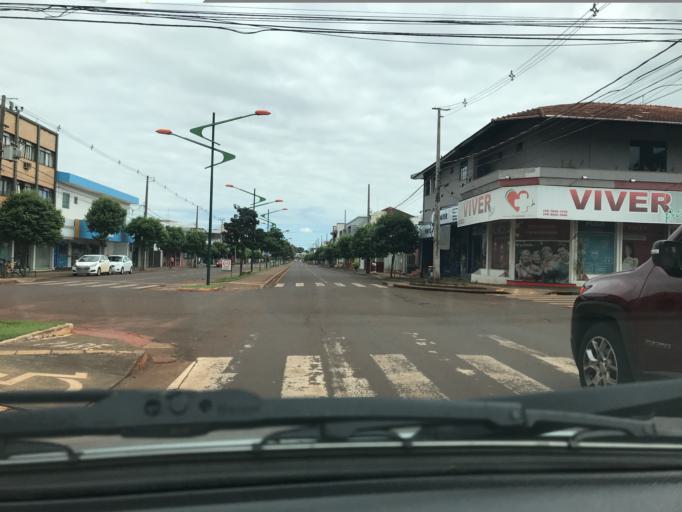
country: BR
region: Parana
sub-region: Palotina
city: Palotina
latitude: -24.2823
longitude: -53.8402
